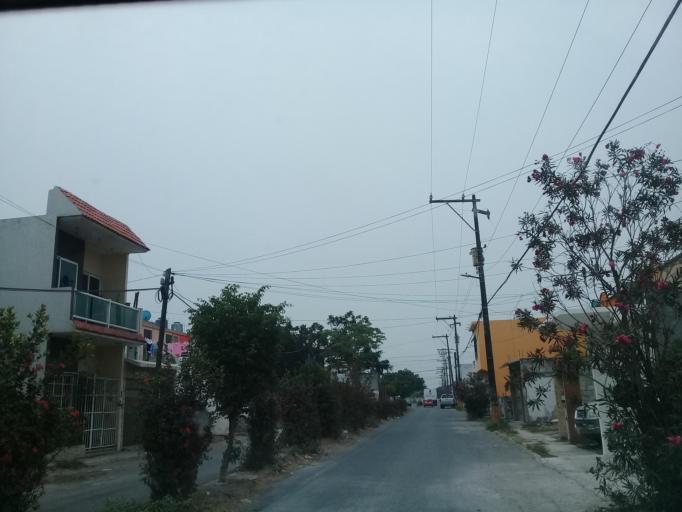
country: MX
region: Veracruz
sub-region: Veracruz
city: Las Amapolas
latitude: 19.1546
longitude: -96.2051
